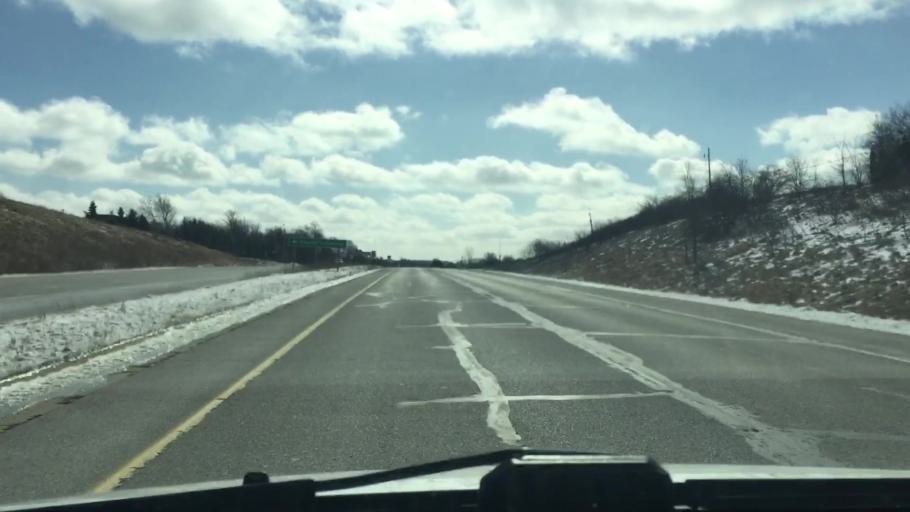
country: US
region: Wisconsin
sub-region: Waukesha County
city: Big Bend
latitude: 42.9356
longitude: -88.2286
